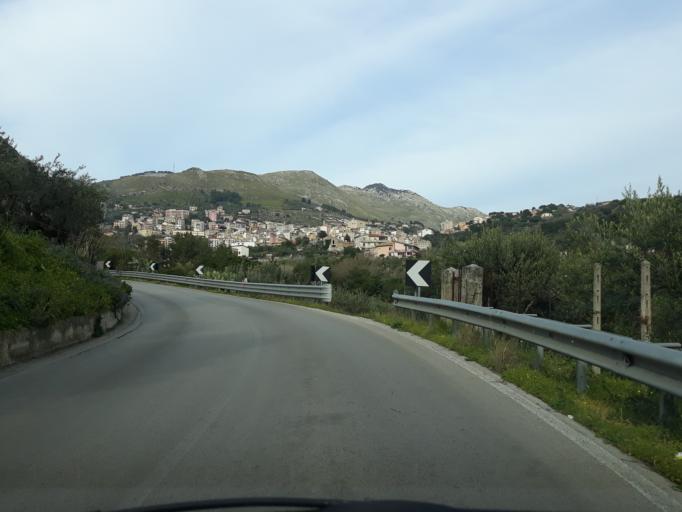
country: IT
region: Sicily
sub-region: Palermo
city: Giardinello
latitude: 38.0812
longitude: 13.1632
